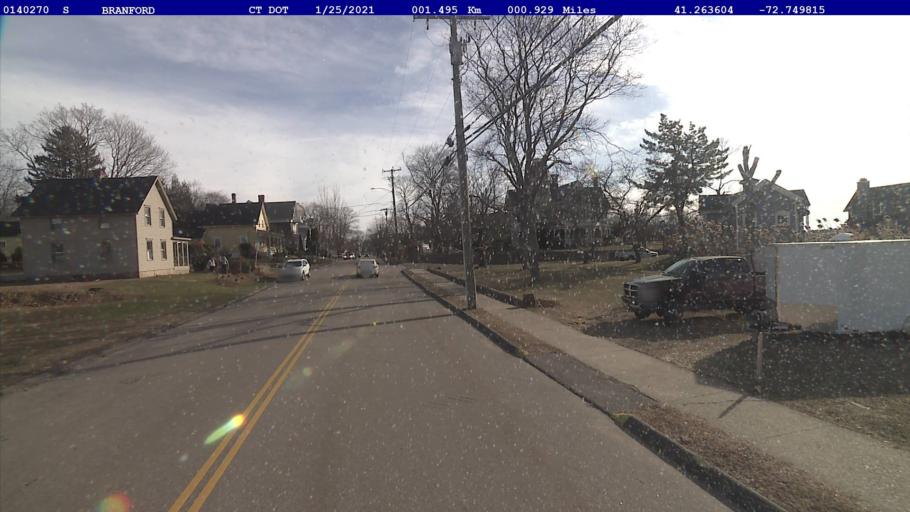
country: US
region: Connecticut
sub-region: New Haven County
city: North Branford
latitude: 41.2636
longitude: -72.7498
